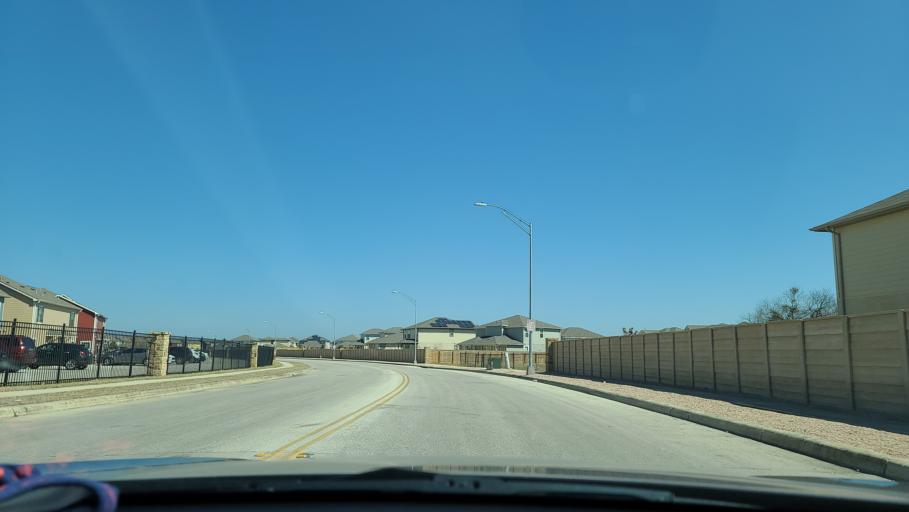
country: US
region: Texas
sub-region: Bexar County
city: Leon Valley
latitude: 29.5628
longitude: -98.6205
